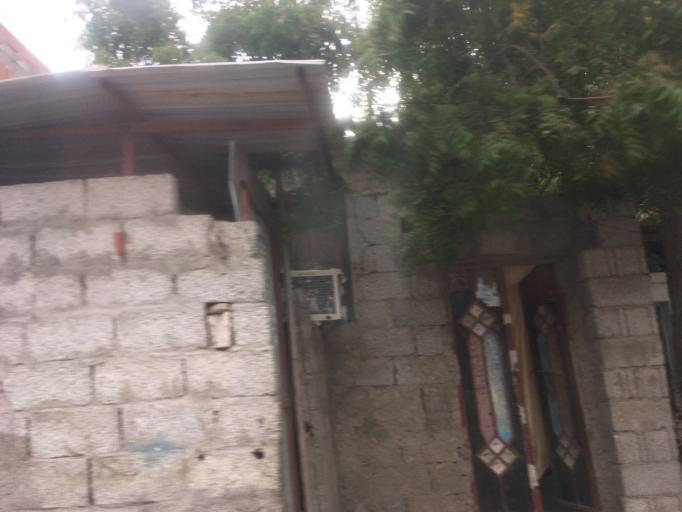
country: YE
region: Aden
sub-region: Al Mansura
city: Al Mansurah
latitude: 12.8571
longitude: 44.9904
